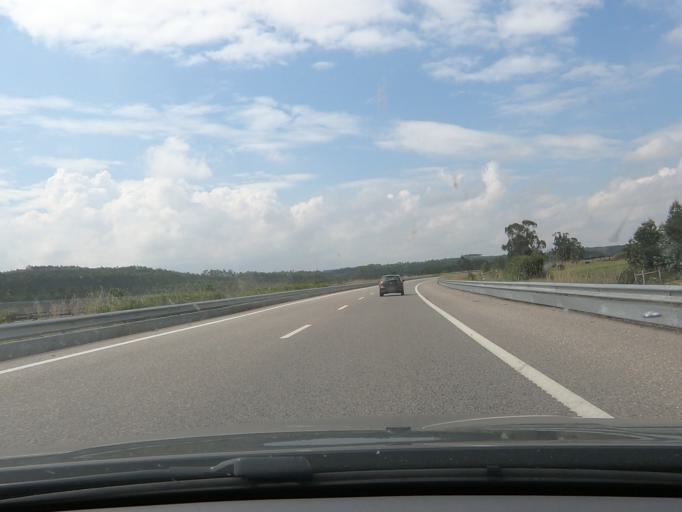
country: PT
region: Leiria
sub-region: Leiria
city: Amor
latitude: 39.7736
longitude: -8.8692
